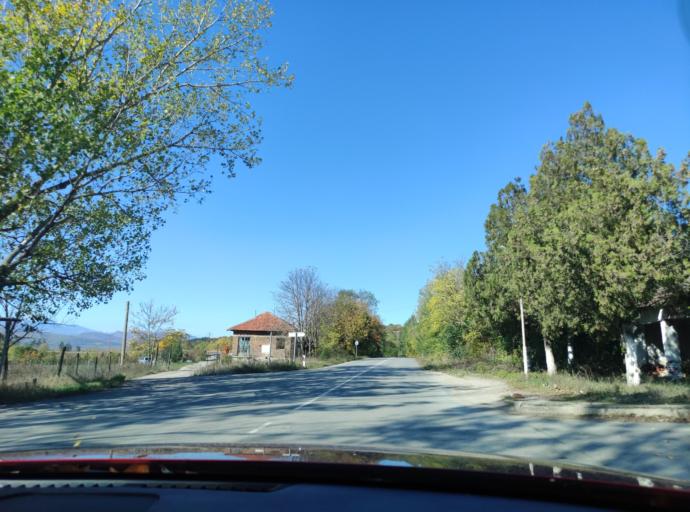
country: BG
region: Montana
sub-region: Obshtina Montana
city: Montana
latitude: 43.3971
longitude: 23.1125
